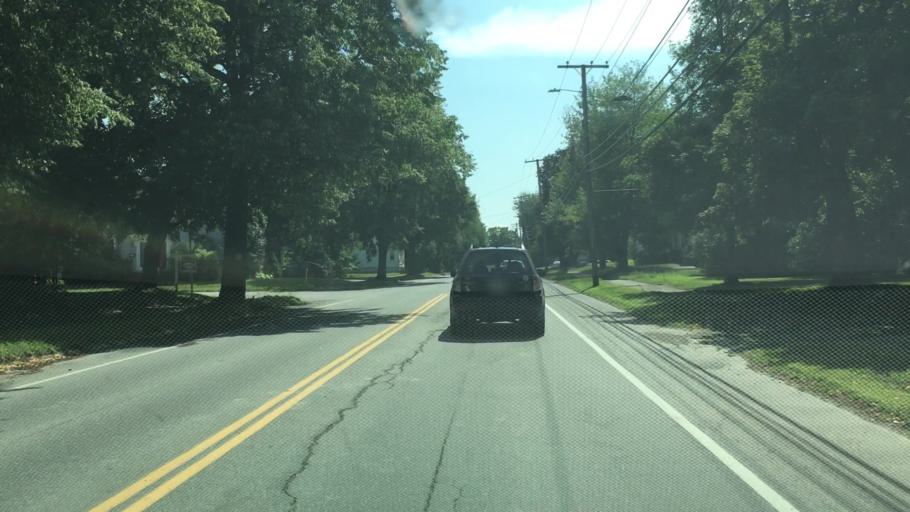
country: US
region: Maine
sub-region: Penobscot County
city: Brewer
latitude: 44.8185
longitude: -68.7634
